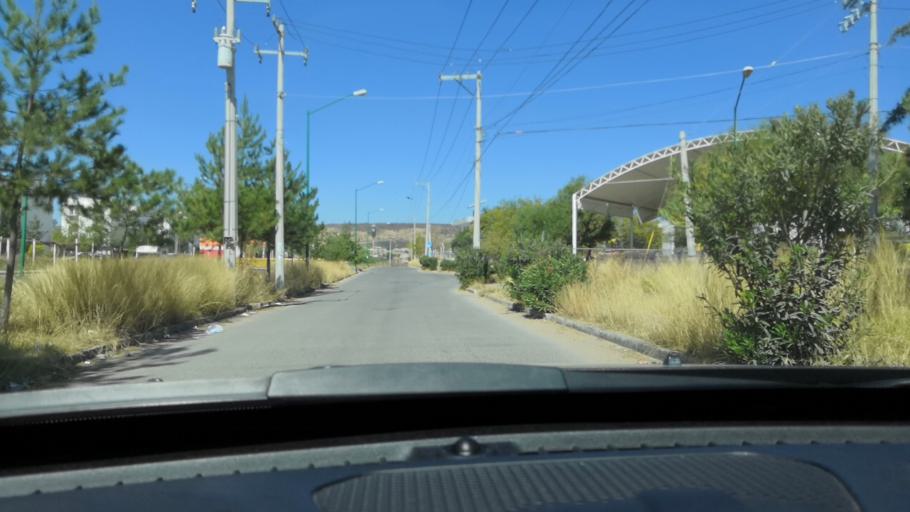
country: MX
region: Guanajuato
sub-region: Leon
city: Centro Familiar la Soledad
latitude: 21.1445
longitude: -101.7516
